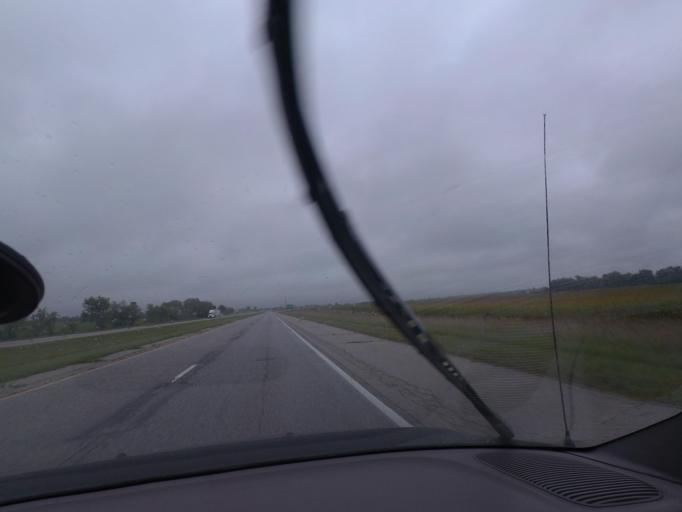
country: US
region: Illinois
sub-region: Pike County
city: Pittsfield
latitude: 39.6724
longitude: -90.8476
